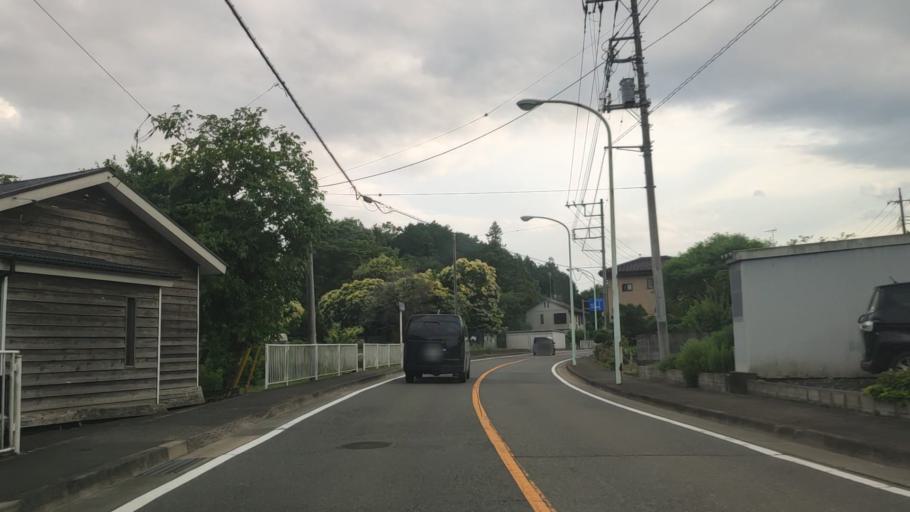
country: JP
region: Saitama
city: Hanno
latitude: 35.8249
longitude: 139.2887
